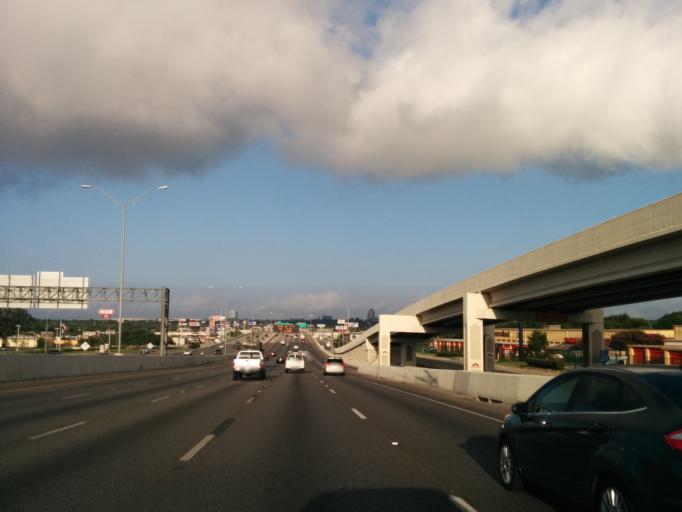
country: US
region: Texas
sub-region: Bexar County
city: Castle Hills
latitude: 29.5189
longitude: -98.5221
